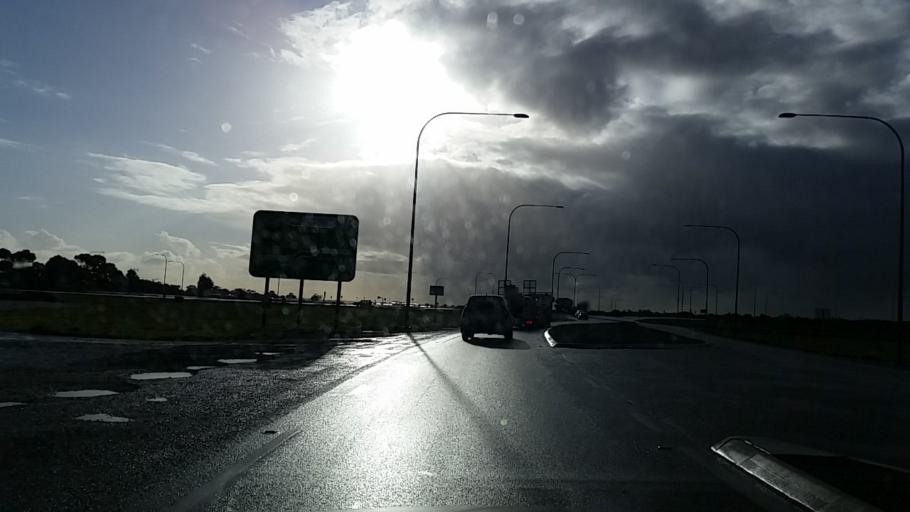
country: AU
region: South Australia
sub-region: Playford
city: Angle Vale
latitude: -34.6833
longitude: 138.6235
